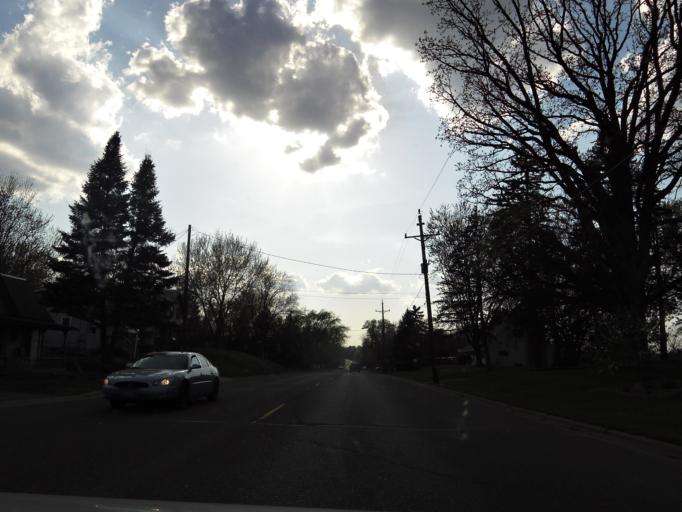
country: US
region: Minnesota
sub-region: Washington County
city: Stillwater
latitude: 45.0530
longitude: -92.8218
